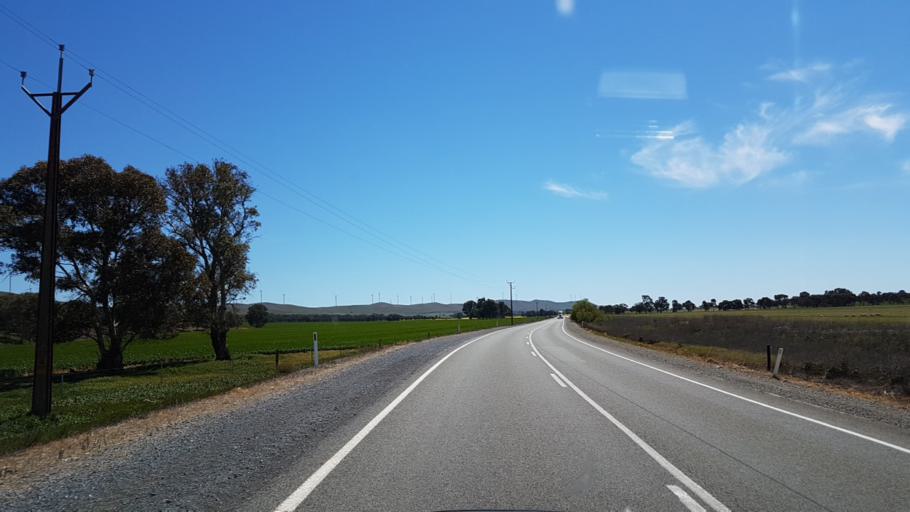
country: AU
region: South Australia
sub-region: Clare and Gilbert Valleys
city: Clare
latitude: -33.6114
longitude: 138.8936
